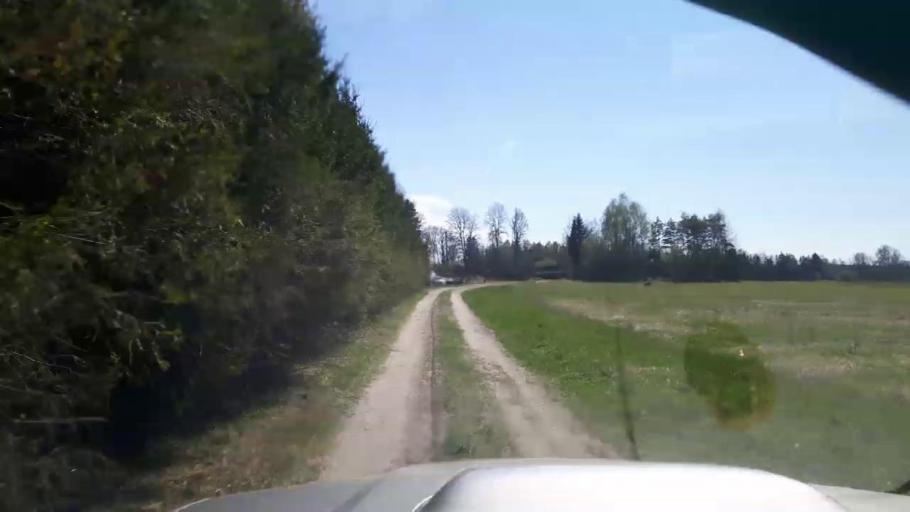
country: EE
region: Paernumaa
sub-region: Tootsi vald
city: Tootsi
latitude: 58.4647
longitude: 24.7991
